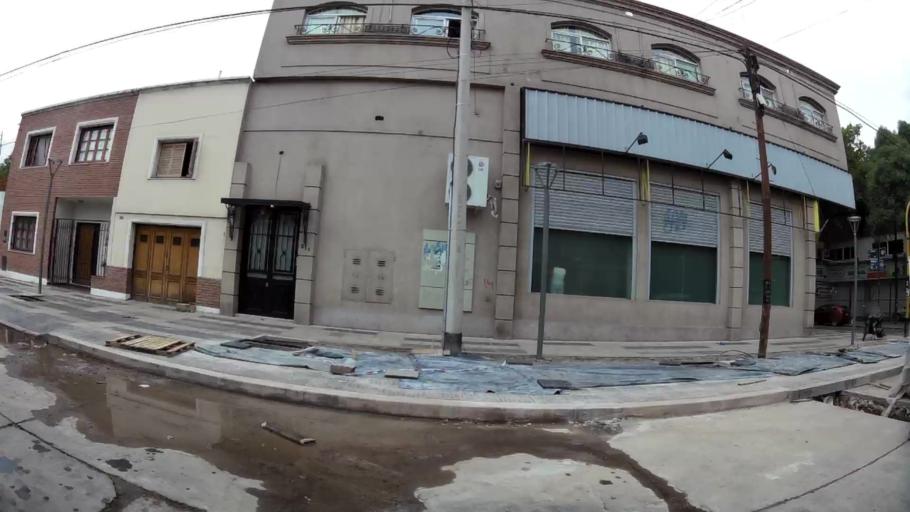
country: AR
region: Mendoza
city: Mendoza
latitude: -32.8826
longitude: -68.8323
